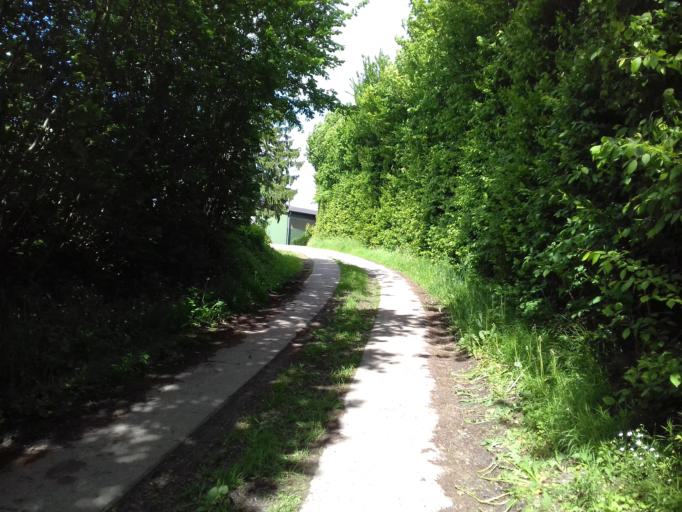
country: DE
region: Schleswig-Holstein
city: Busdorf
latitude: 54.1150
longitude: 10.1008
